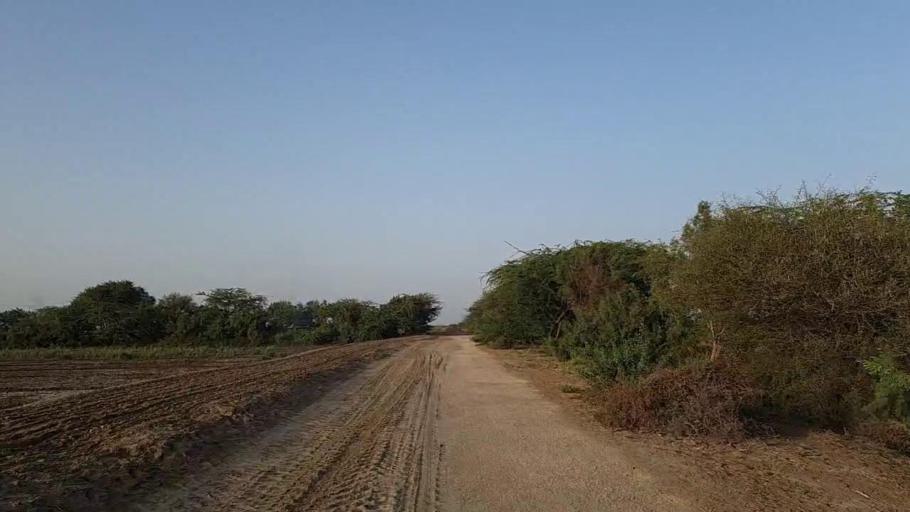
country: PK
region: Sindh
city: Jati
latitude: 24.4180
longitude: 68.1909
